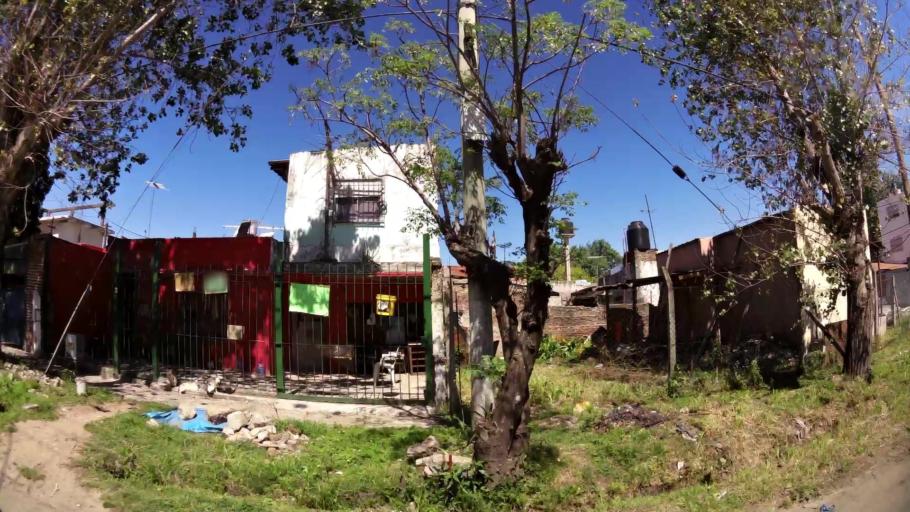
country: AR
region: Buenos Aires
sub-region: Partido de Quilmes
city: Quilmes
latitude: -34.7313
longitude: -58.3108
